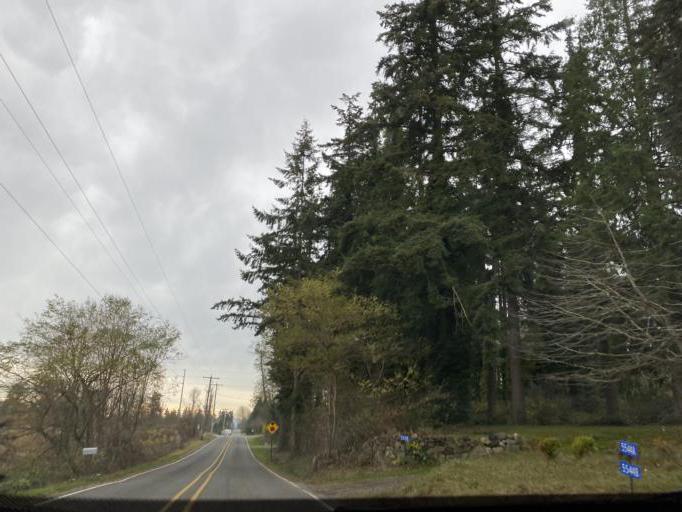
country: US
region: Washington
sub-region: Island County
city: Freeland
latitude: 48.0106
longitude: -122.5070
